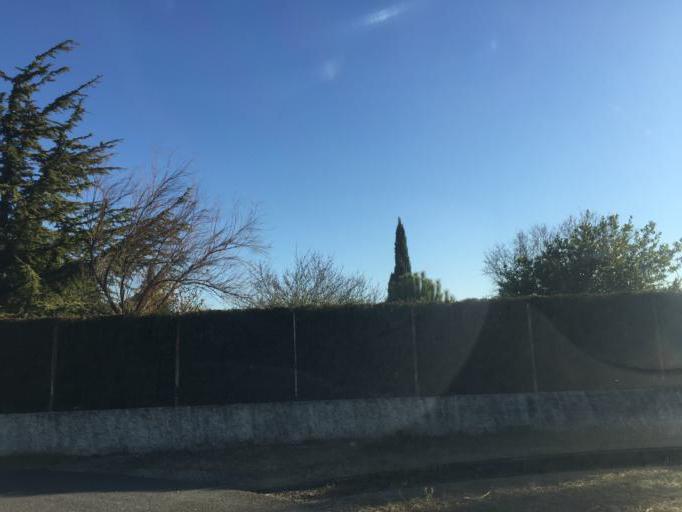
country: FR
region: Provence-Alpes-Cote d'Azur
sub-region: Departement du Vaucluse
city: Orange
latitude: 44.1494
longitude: 4.8151
